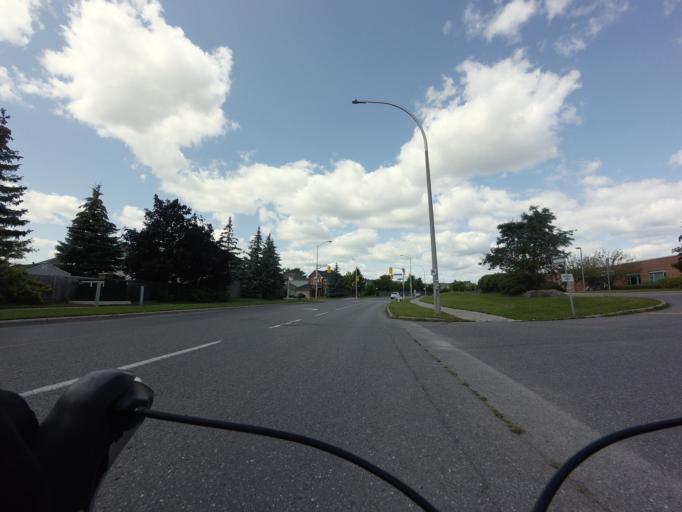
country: CA
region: Ontario
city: Bells Corners
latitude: 45.2814
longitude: -75.8442
